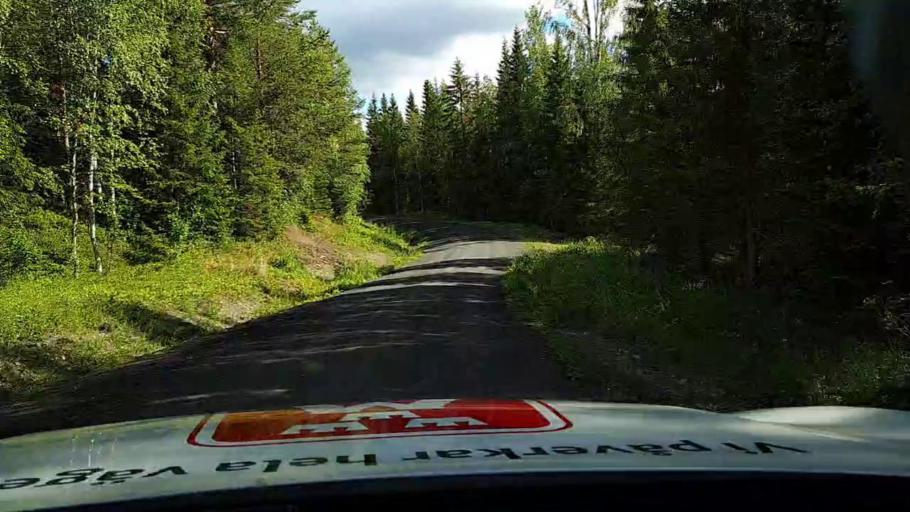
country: SE
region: Jaemtland
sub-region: Krokoms Kommun
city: Valla
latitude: 63.3224
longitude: 13.7550
